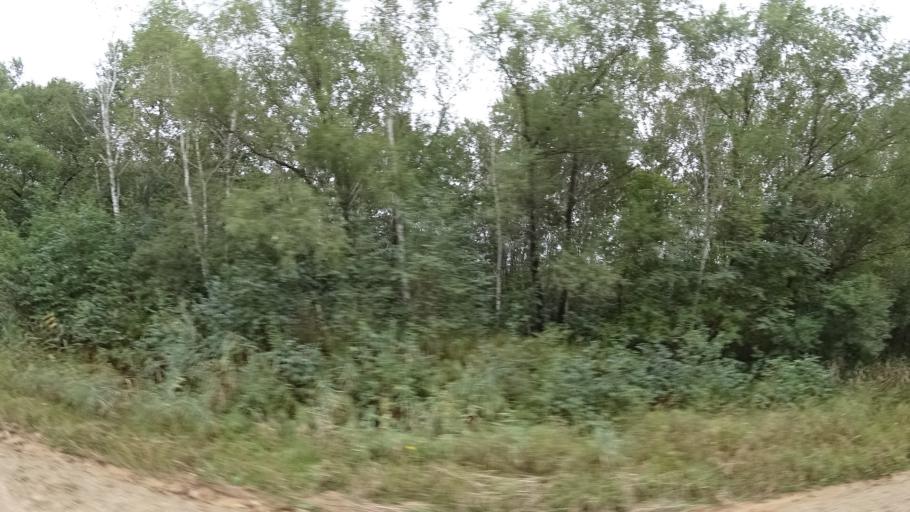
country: RU
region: Primorskiy
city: Rettikhovka
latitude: 44.1470
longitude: 132.6762
